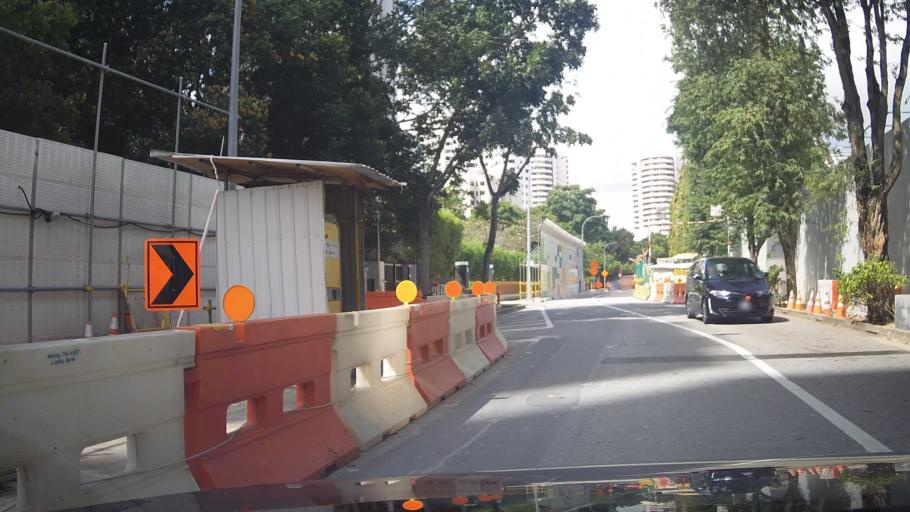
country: SG
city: Singapore
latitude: 1.2979
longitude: 103.8940
